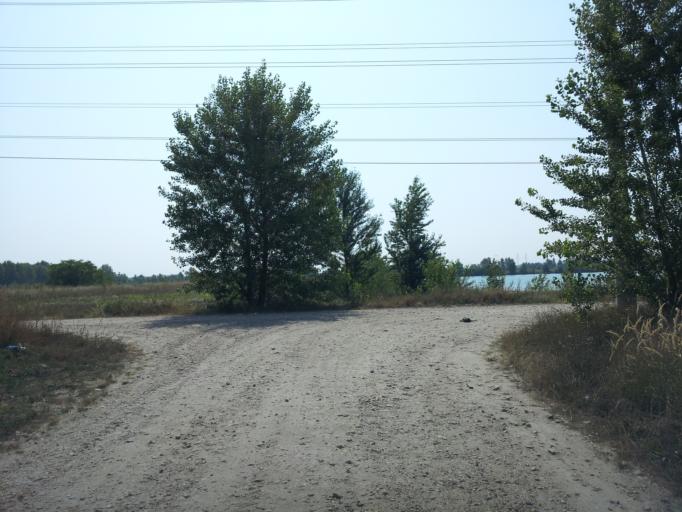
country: HU
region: Pest
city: Dunavarsany
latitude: 47.2815
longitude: 19.0428
